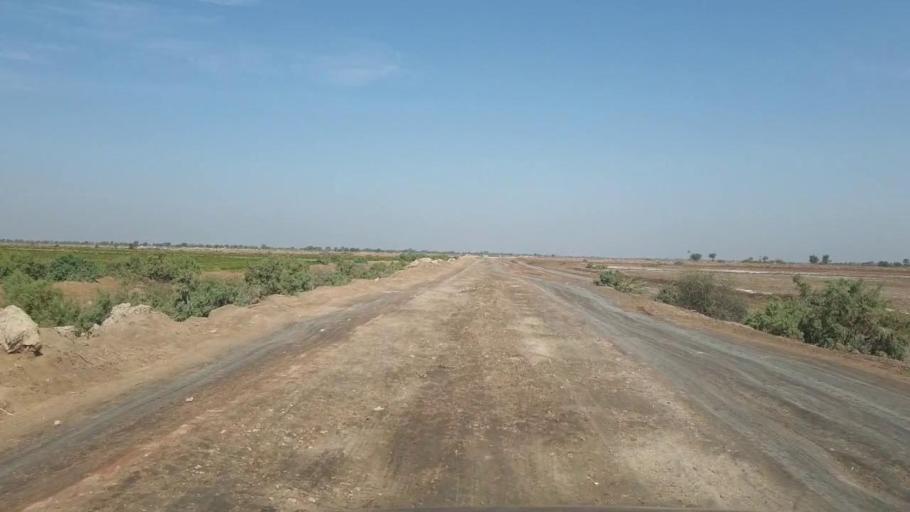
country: PK
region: Sindh
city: Samaro
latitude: 25.3562
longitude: 69.2537
